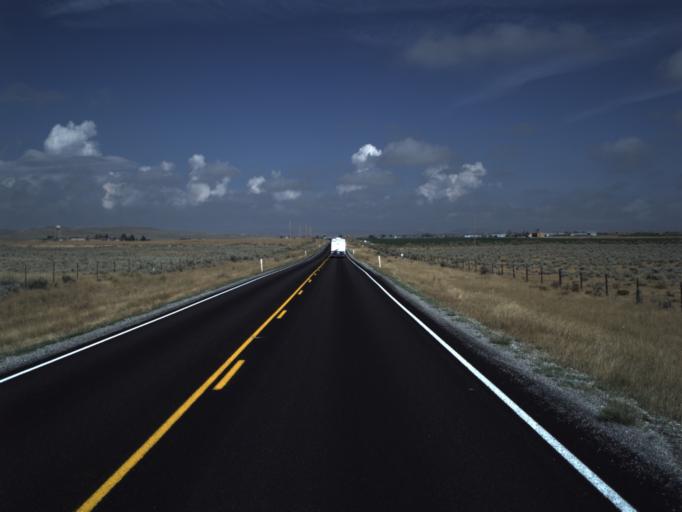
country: US
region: Utah
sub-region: Rich County
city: Randolph
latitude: 41.5733
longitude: -111.1624
